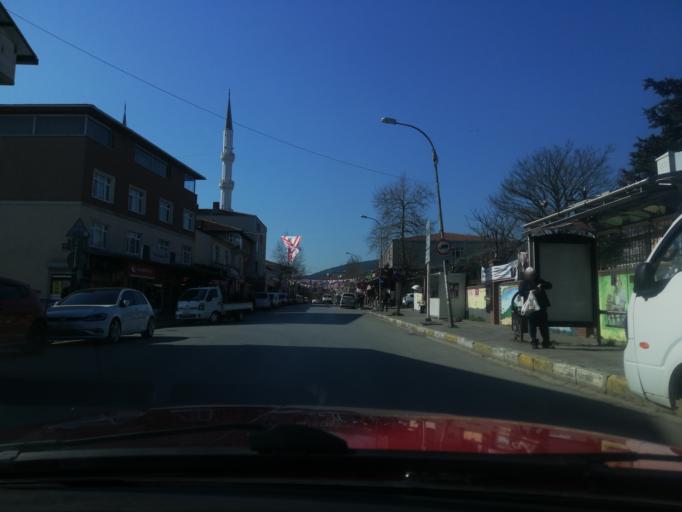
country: TR
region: Istanbul
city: Umraniye
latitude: 41.0805
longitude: 29.1405
